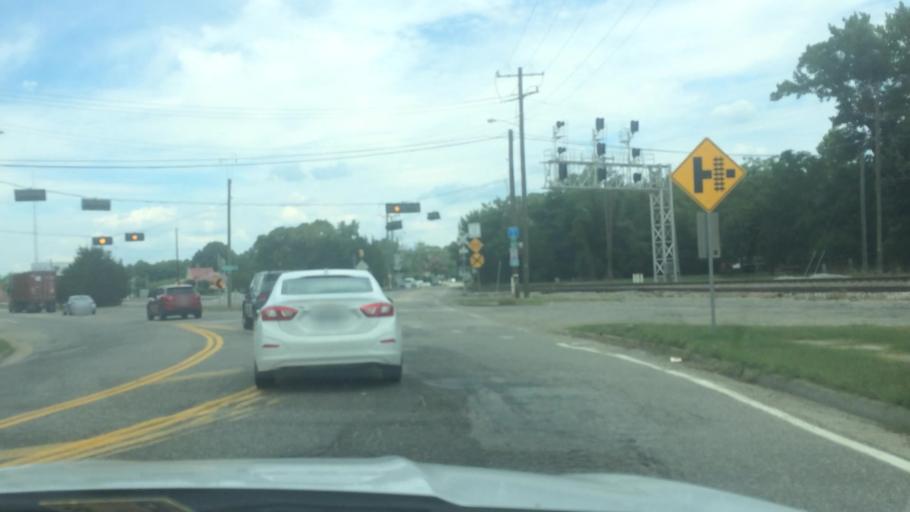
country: US
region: Virginia
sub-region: York County
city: Yorktown
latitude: 37.1915
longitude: -76.5715
